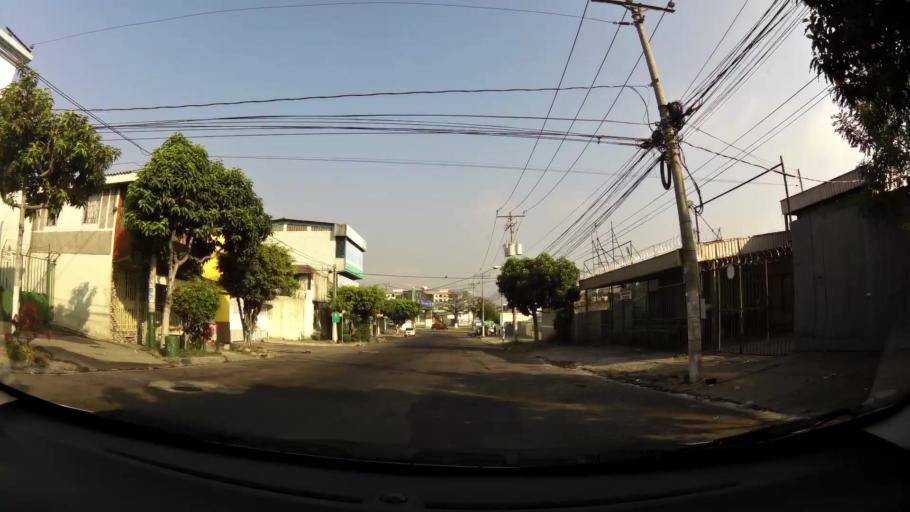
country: SV
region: San Salvador
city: San Salvador
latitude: 13.6835
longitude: -89.2191
